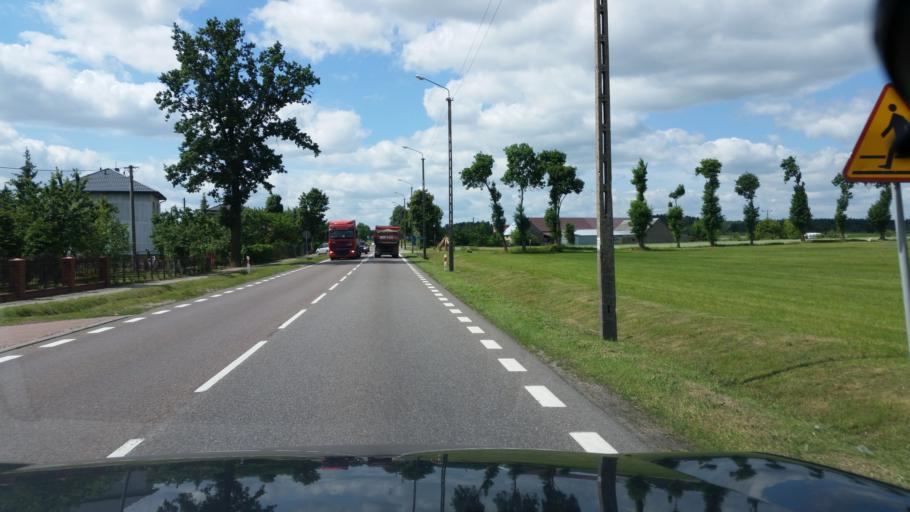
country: PL
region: Podlasie
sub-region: Powiat grajewski
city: Grajewo
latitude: 53.6219
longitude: 22.3997
